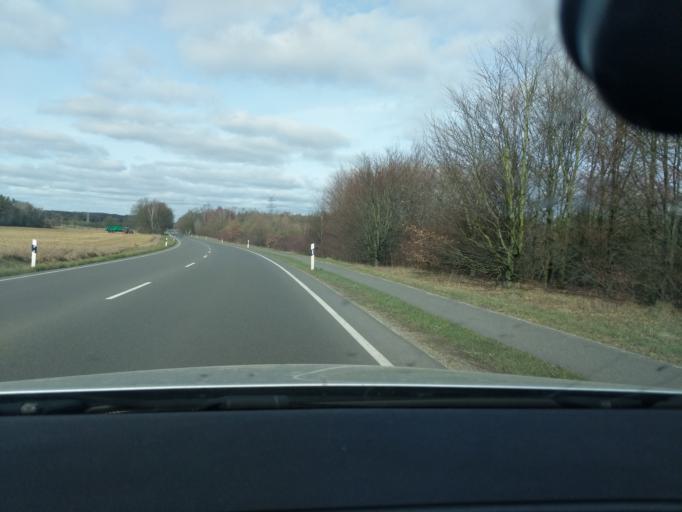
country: DE
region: Lower Saxony
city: Dollern
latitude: 53.5463
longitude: 9.5429
